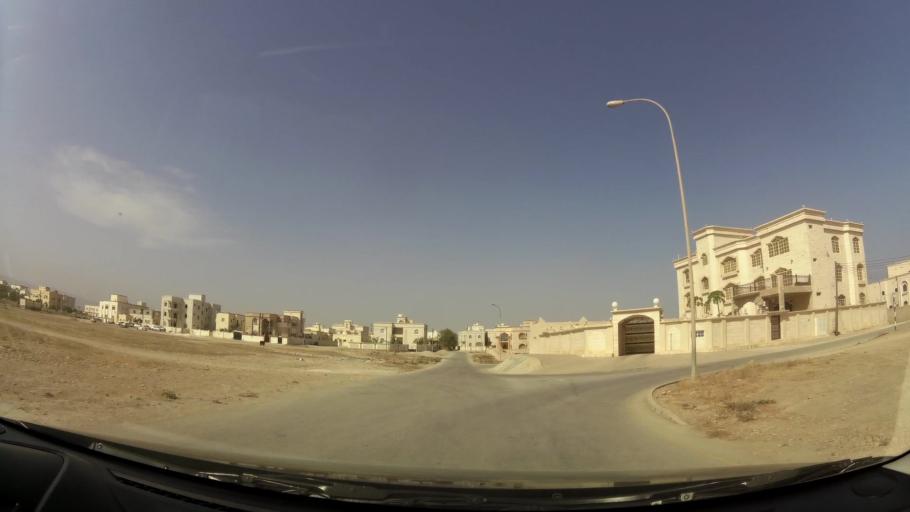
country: OM
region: Zufar
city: Salalah
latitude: 17.0012
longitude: 54.0145
